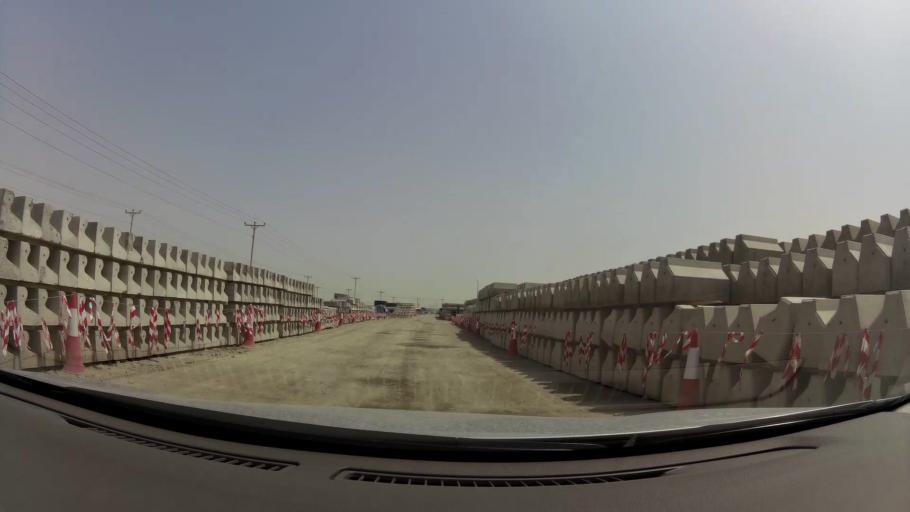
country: QA
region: Baladiyat ar Rayyan
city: Ar Rayyan
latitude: 25.1803
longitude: 51.4220
